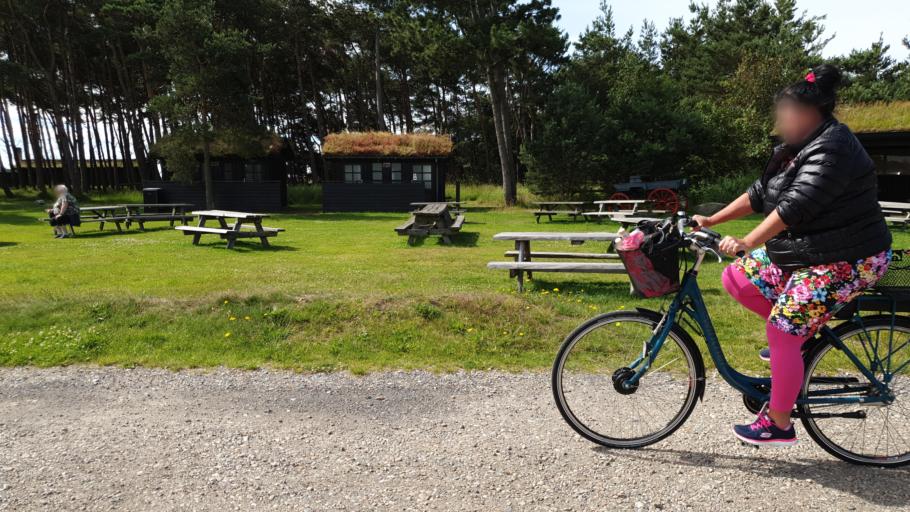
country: DK
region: North Denmark
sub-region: Laeso Kommune
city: Byrum
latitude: 57.2400
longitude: 10.9896
